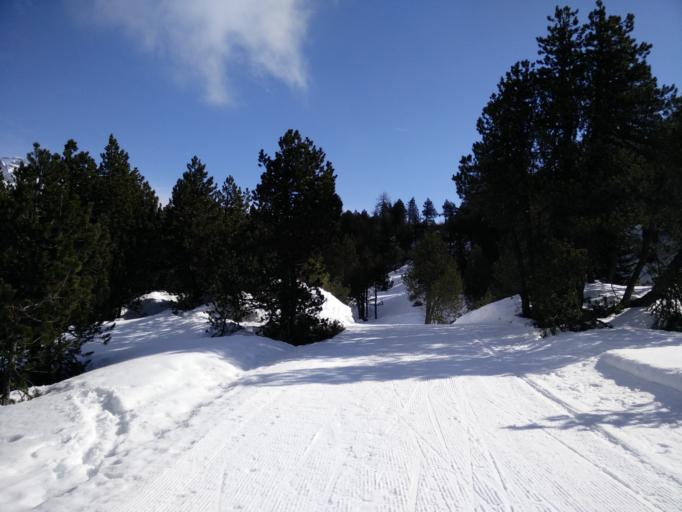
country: CH
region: Grisons
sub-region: Maloja District
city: Silvaplana
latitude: 46.3994
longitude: 9.6993
